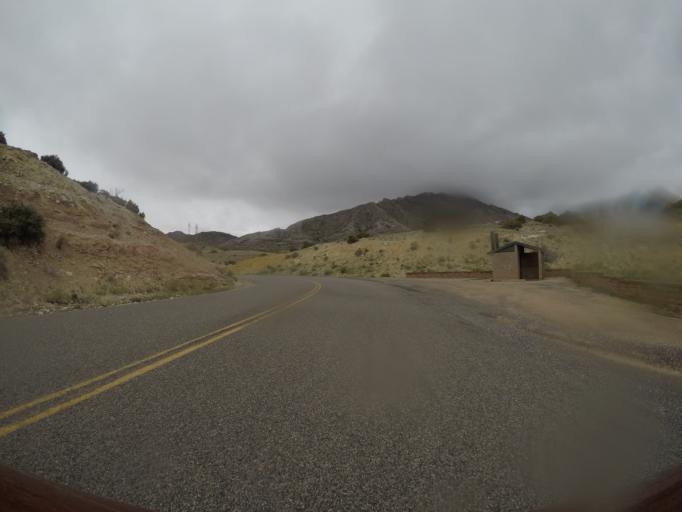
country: US
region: Wyoming
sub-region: Big Horn County
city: Lovell
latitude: 45.0261
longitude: -108.2646
